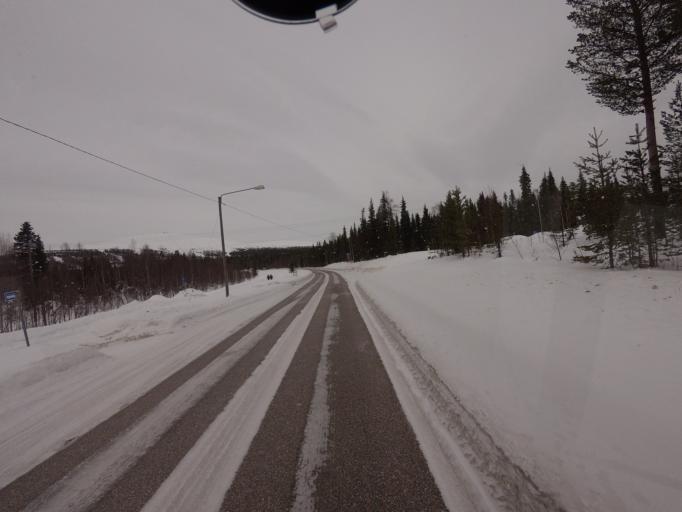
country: FI
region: Lapland
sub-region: Tunturi-Lappi
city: Kolari
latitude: 67.5352
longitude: 24.2767
